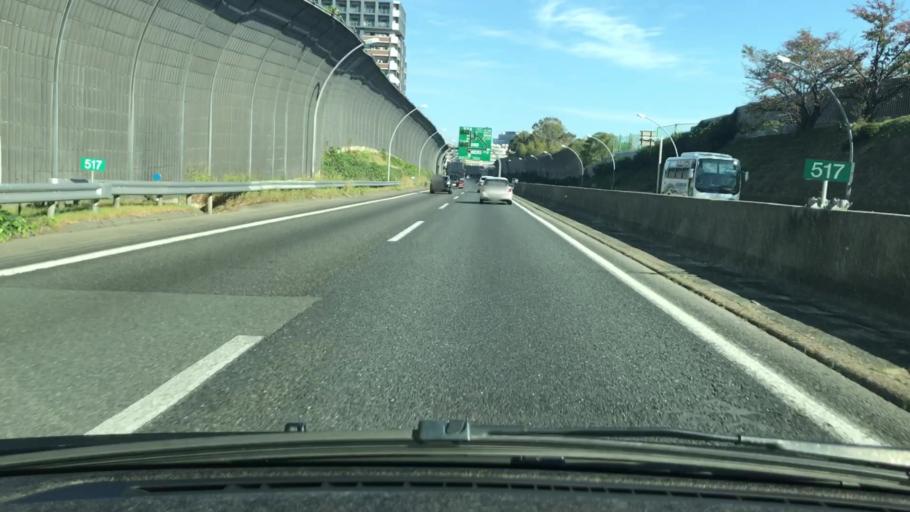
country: JP
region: Osaka
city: Suita
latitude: 34.7883
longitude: 135.5322
